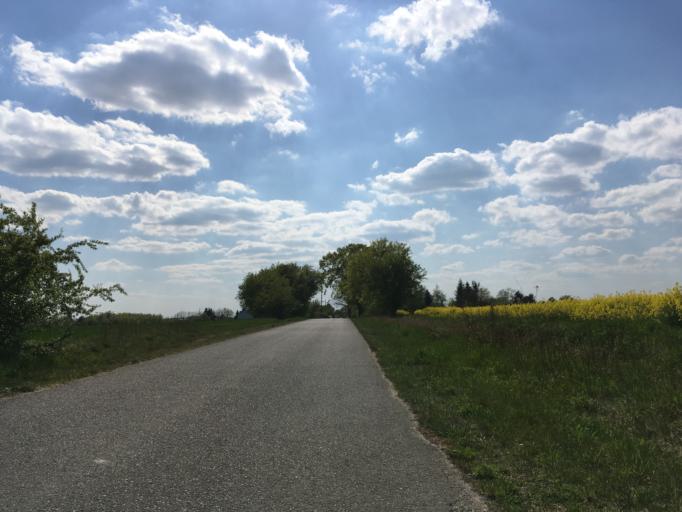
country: DE
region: Brandenburg
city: Ahrensfelde
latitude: 52.6097
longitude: 13.6096
